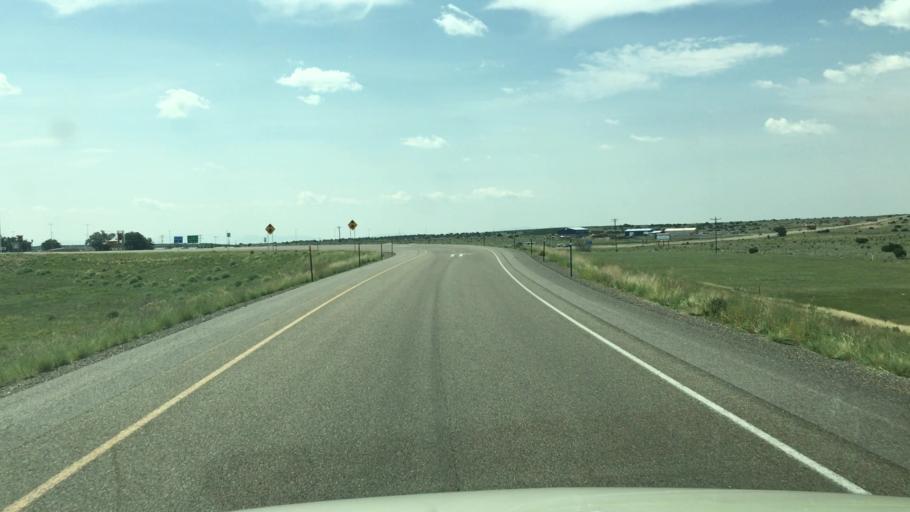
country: US
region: New Mexico
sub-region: Torrance County
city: Moriarty
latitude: 35.0092
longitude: -105.6625
